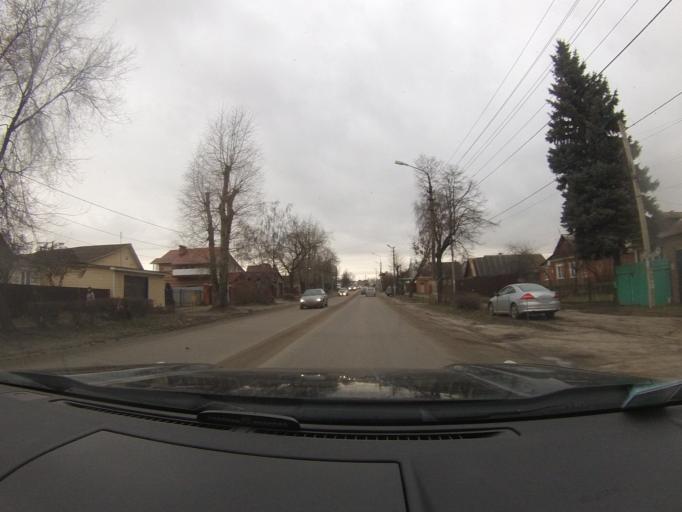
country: RU
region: Moskovskaya
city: Lopatinskiy
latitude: 55.3259
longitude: 38.6933
